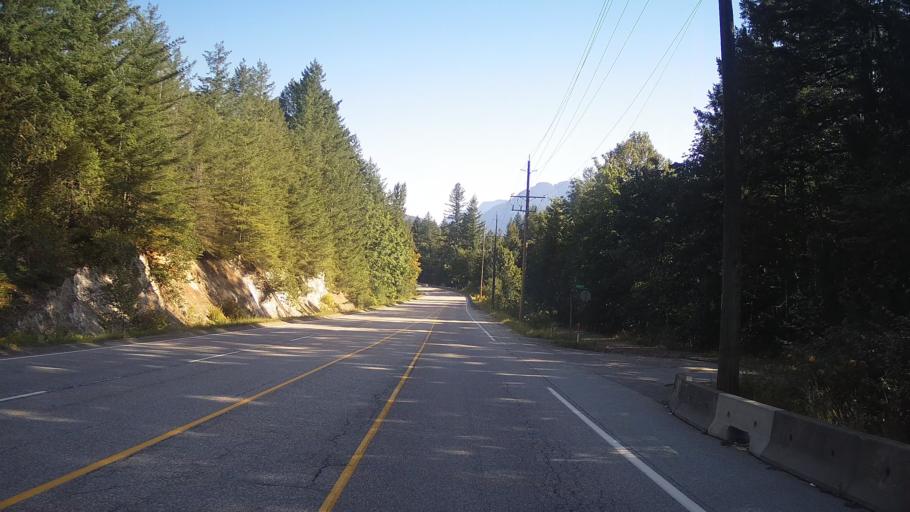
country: CA
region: British Columbia
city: Hope
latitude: 49.4264
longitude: -121.4382
